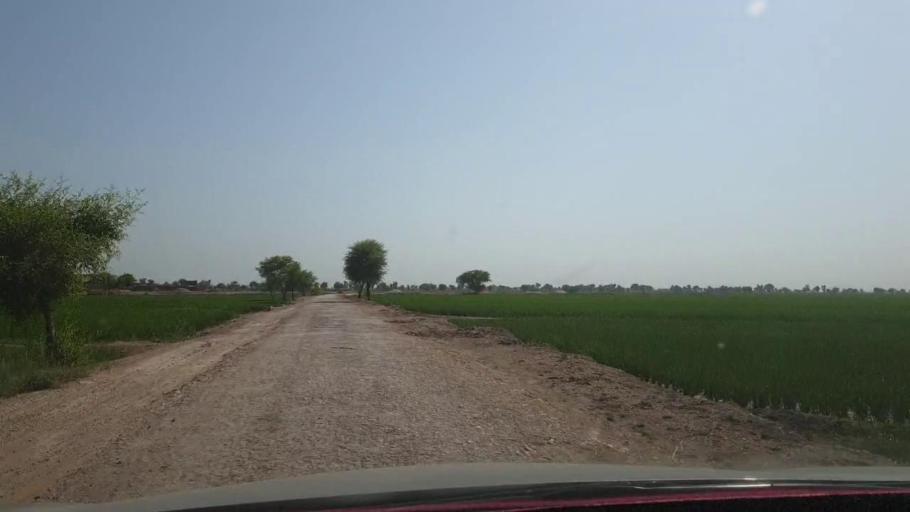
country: PK
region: Sindh
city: Nasirabad
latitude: 27.3595
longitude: 67.8504
